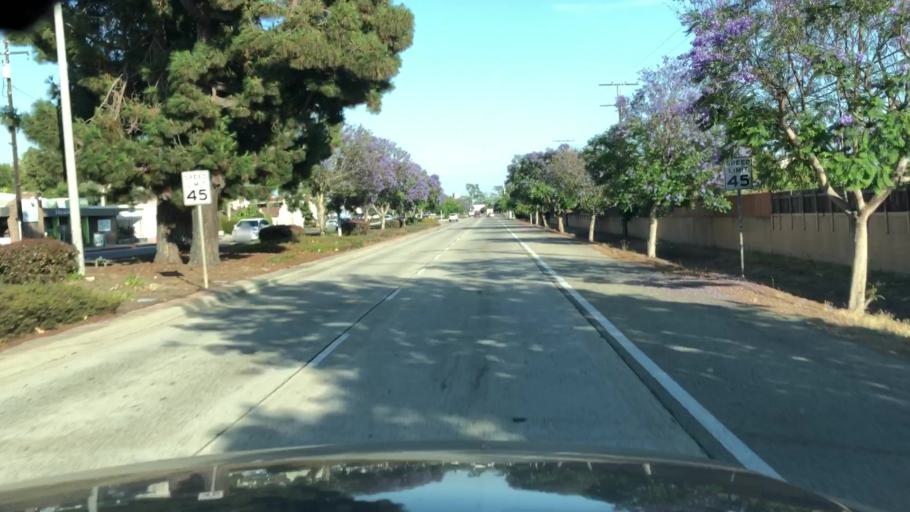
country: US
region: California
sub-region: Ventura County
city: Ventura
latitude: 34.2683
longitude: -119.2523
